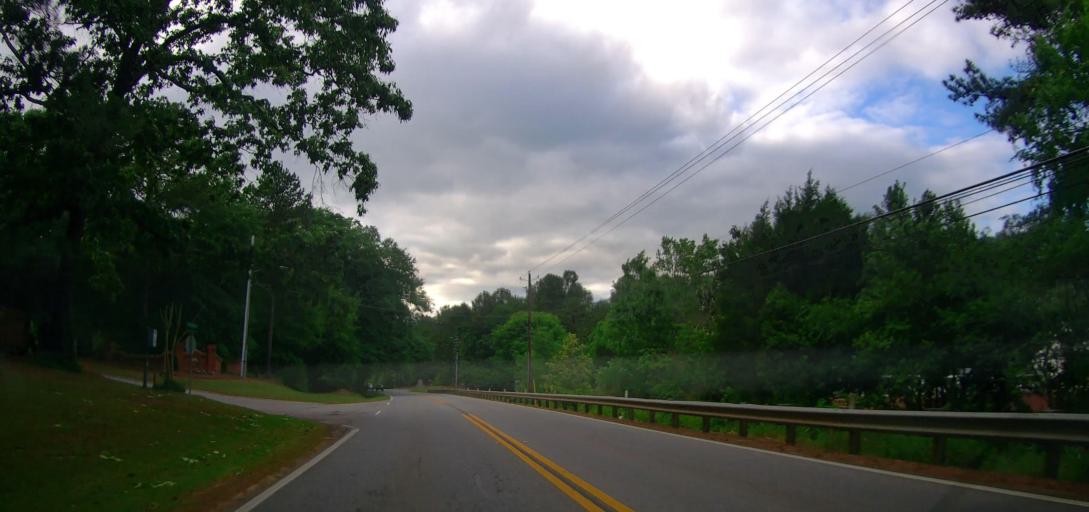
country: US
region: Georgia
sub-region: Clarke County
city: Athens
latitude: 33.9275
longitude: -83.4124
